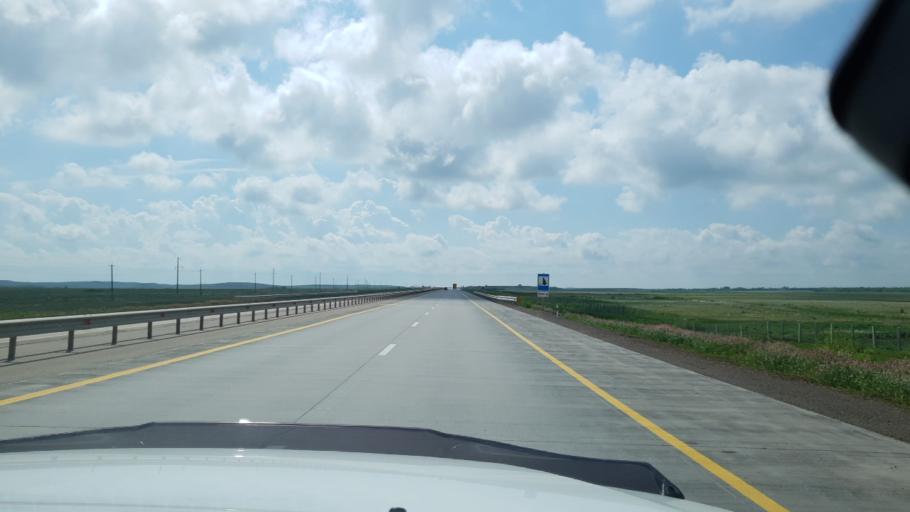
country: KZ
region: Qaraghandy
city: Osakarovka
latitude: 50.8013
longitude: 72.2062
